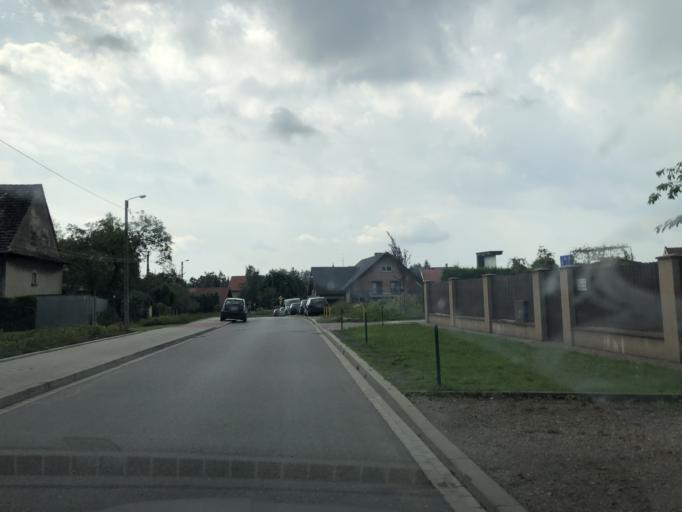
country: PL
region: Lesser Poland Voivodeship
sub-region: Powiat krakowski
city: Libertow
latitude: 50.0053
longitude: 19.9262
